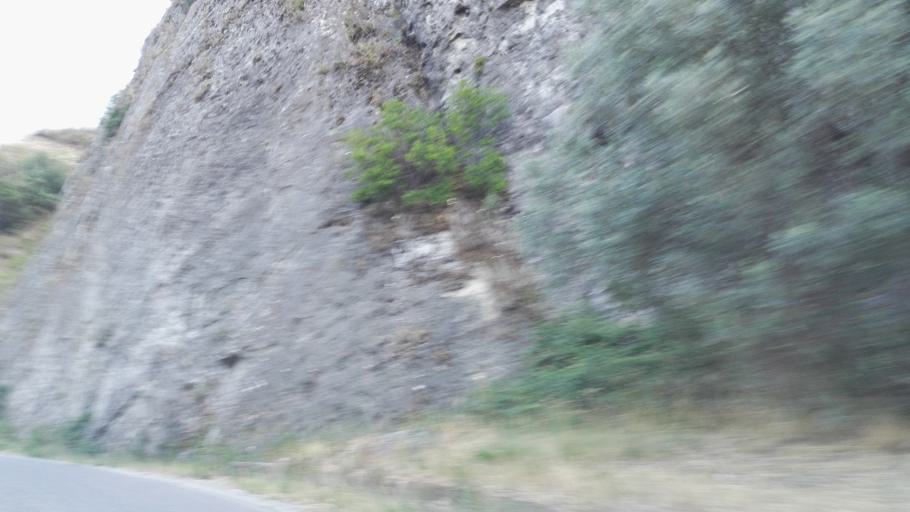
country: IT
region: Calabria
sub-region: Provincia di Reggio Calabria
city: Caulonia
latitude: 38.4013
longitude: 16.4103
